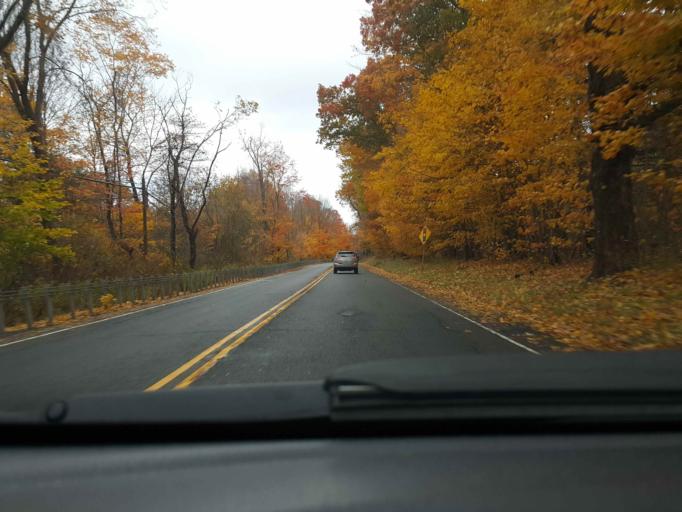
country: US
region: Connecticut
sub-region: Middlesex County
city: Durham
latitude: 41.5208
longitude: -72.6676
